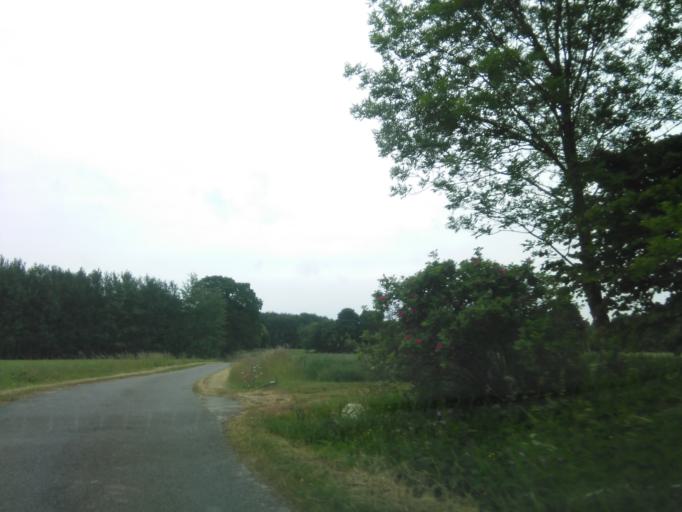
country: DK
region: Capital Region
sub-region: Bornholm Kommune
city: Akirkeby
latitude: 55.1156
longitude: 14.9238
